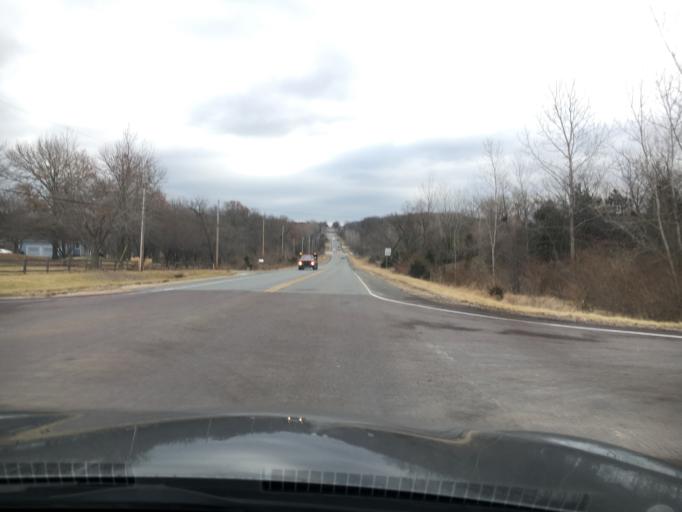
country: US
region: Kansas
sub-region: Johnson County
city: Spring Hill
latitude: 38.8036
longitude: -94.6867
